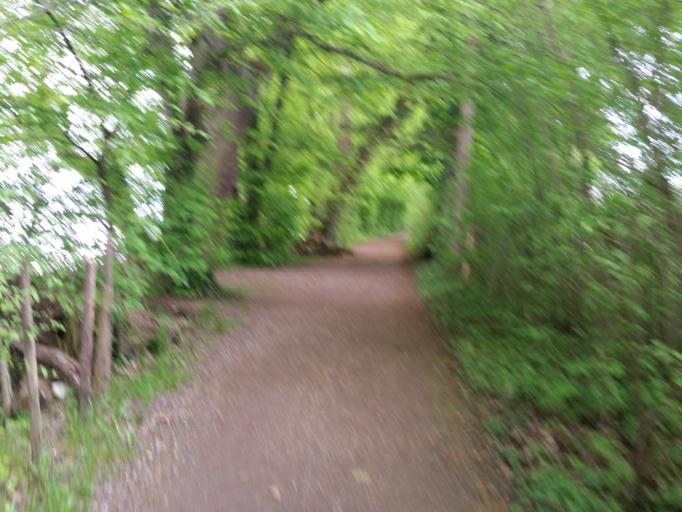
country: CH
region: Thurgau
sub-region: Kreuzlingen District
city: Guttingen
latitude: 47.6030
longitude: 9.3103
